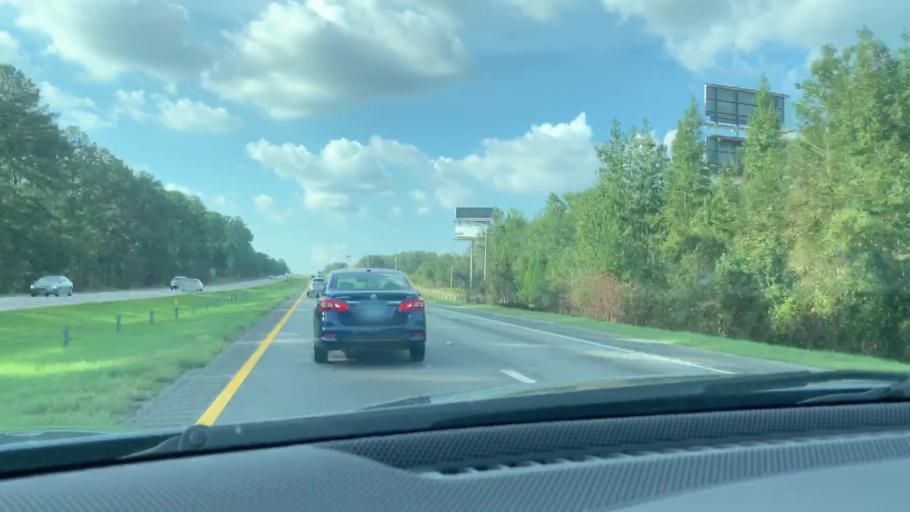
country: US
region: South Carolina
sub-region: Calhoun County
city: Saint Matthews
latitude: 33.6627
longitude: -80.8910
